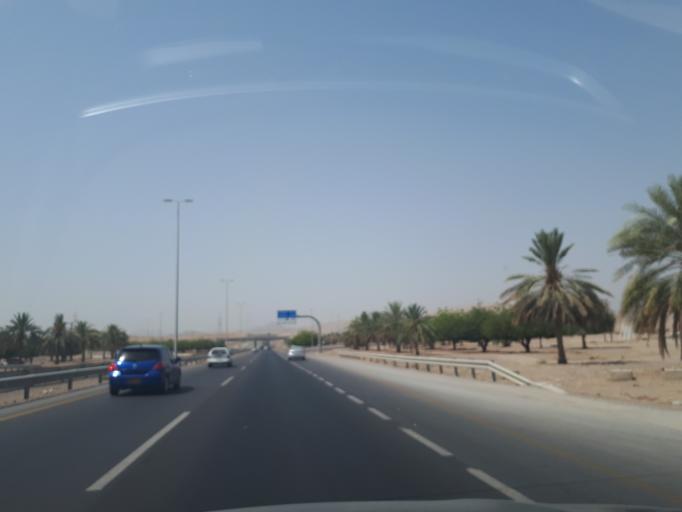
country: OM
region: Muhafazat Masqat
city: As Sib al Jadidah
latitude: 23.5772
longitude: 58.1940
